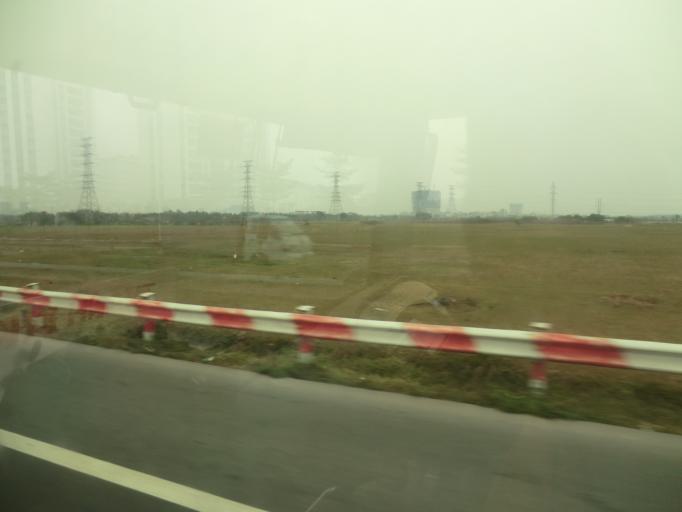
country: VN
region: Ha Noi
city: Van Dien
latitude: 20.9512
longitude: 105.8540
